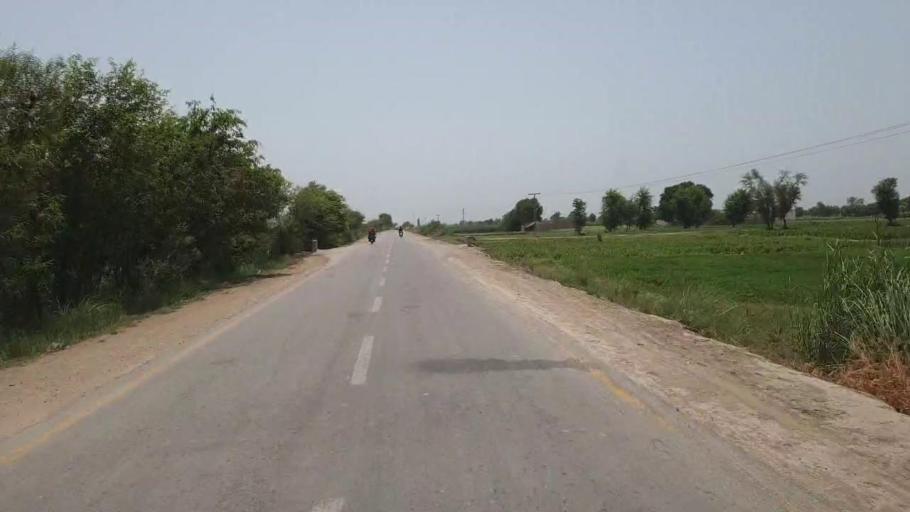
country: PK
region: Sindh
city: Moro
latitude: 26.5998
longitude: 68.0899
